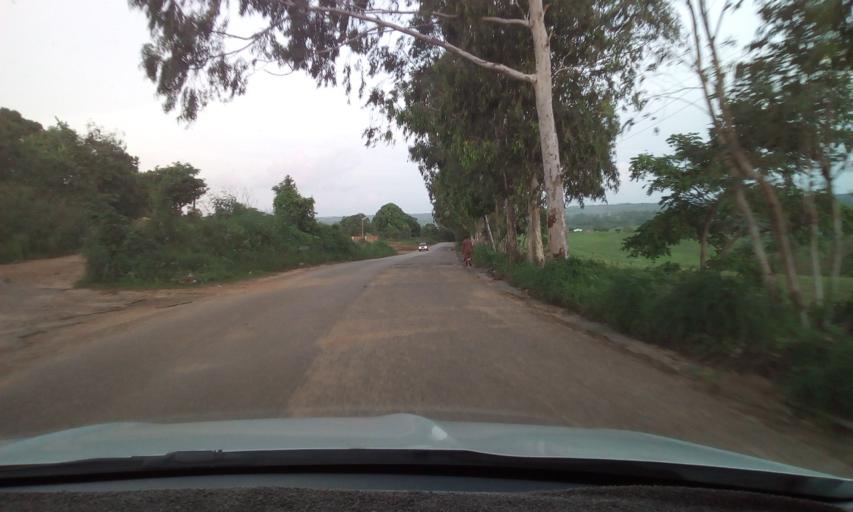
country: BR
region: Pernambuco
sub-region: Vicencia
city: Vicencia
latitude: -7.5964
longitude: -35.2277
